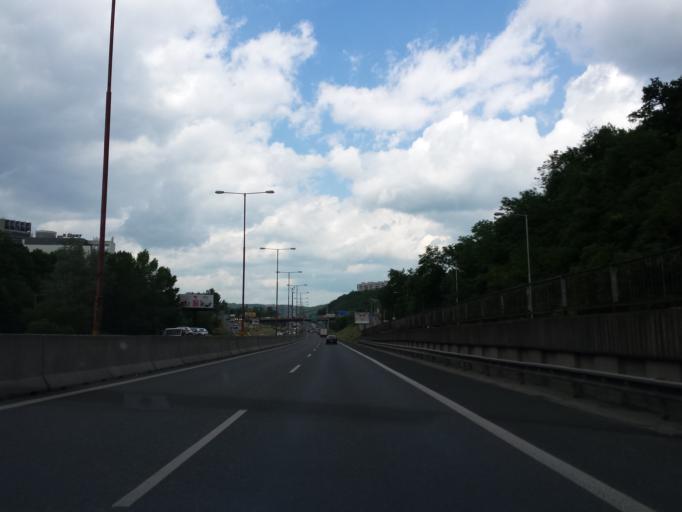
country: SK
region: Bratislavsky
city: Bratislava
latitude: 48.1501
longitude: 17.0764
